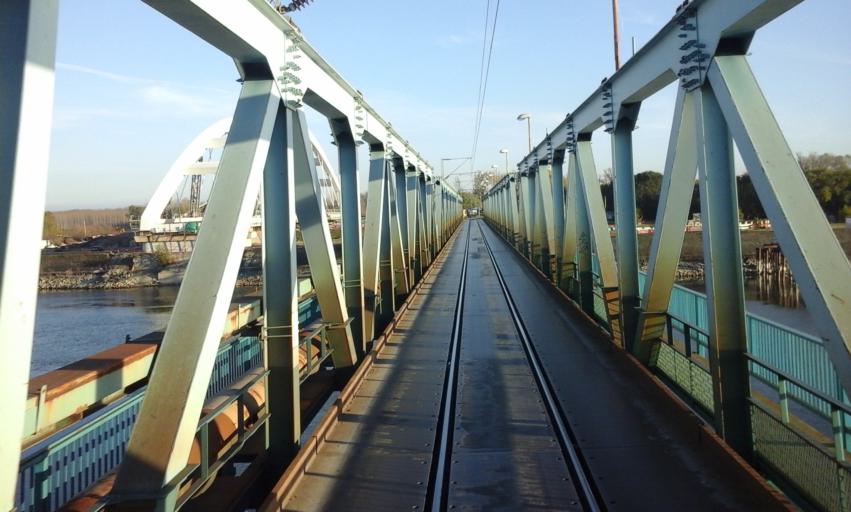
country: RS
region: Autonomna Pokrajina Vojvodina
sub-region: Juznobacki Okrug
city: Novi Sad
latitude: 45.2616
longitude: 19.8596
